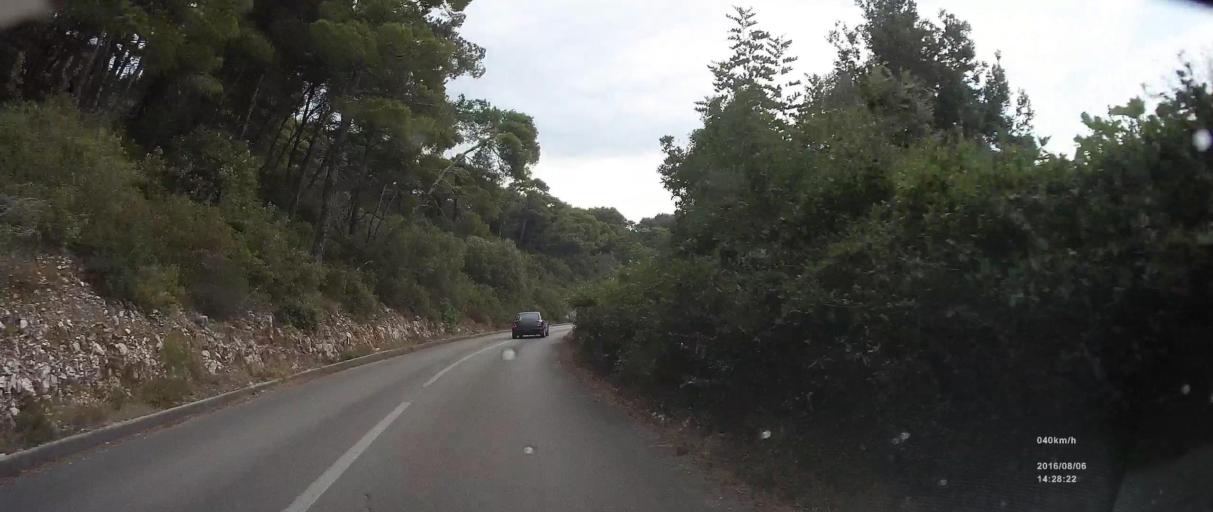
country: HR
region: Dubrovacko-Neretvanska
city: Ston
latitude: 42.7033
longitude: 17.7363
